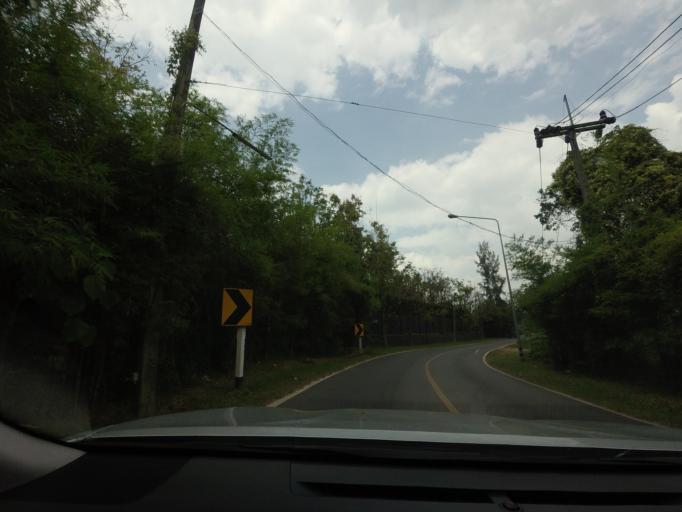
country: TH
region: Phangnga
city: Ban Ao Nang
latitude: 8.0855
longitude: 98.7456
